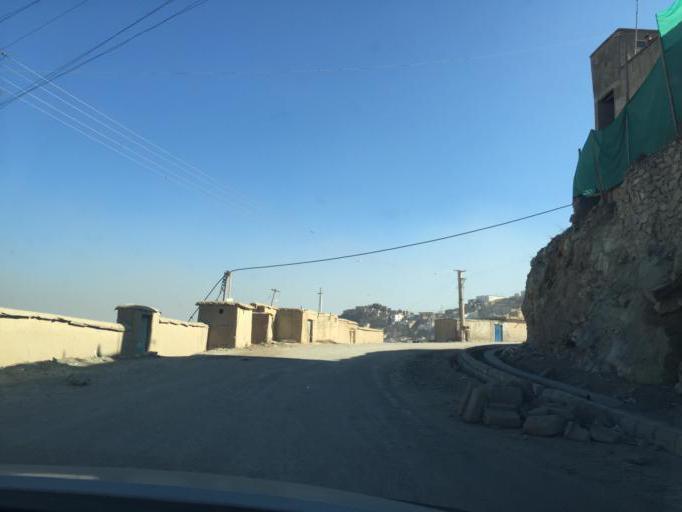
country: AF
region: Kabul
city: Kabul
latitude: 34.5253
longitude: 69.1528
